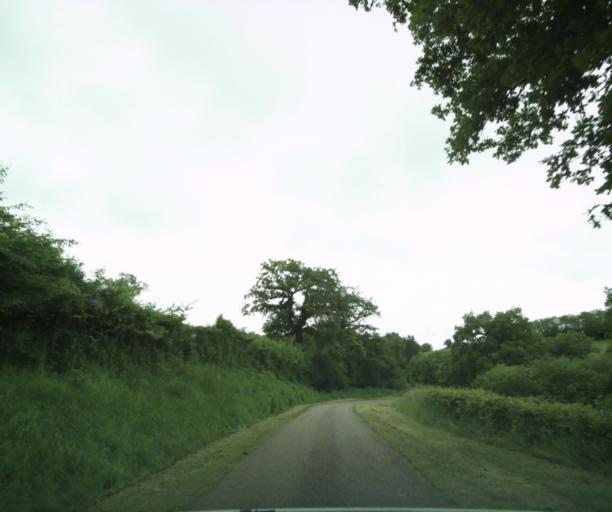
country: FR
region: Bourgogne
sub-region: Departement de Saone-et-Loire
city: Charolles
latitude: 46.4664
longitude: 4.2905
